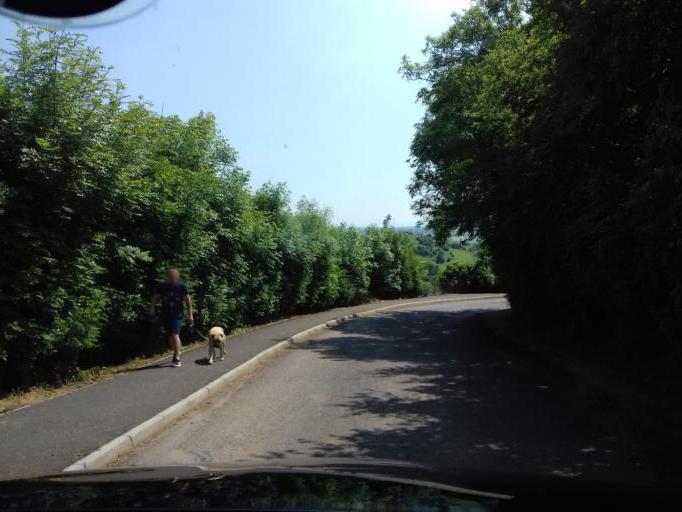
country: IE
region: Leinster
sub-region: An Mhi
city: Slane
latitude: 53.7161
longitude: -6.5377
